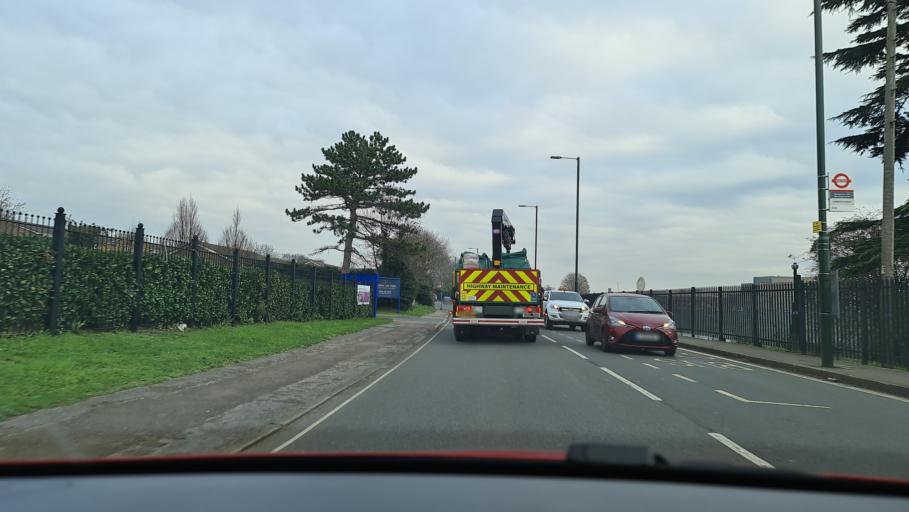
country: GB
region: England
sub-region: Greater London
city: Hampton
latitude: 51.4135
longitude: -0.3788
